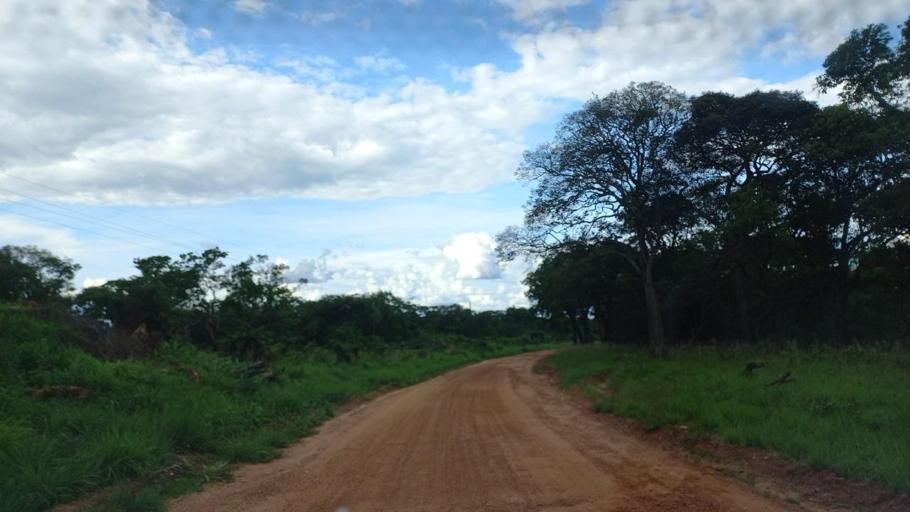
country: ZM
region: North-Western
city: Mwinilunga
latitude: -11.8185
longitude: 24.3641
